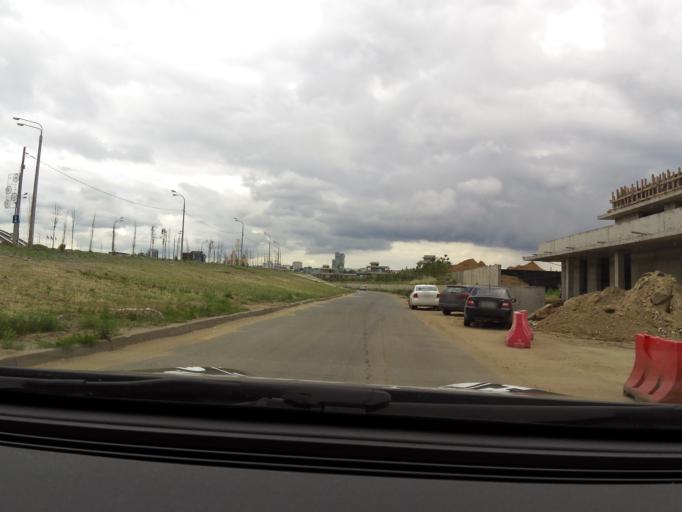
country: RU
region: Tatarstan
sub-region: Gorod Kazan'
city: Kazan
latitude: 55.8134
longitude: 49.1330
